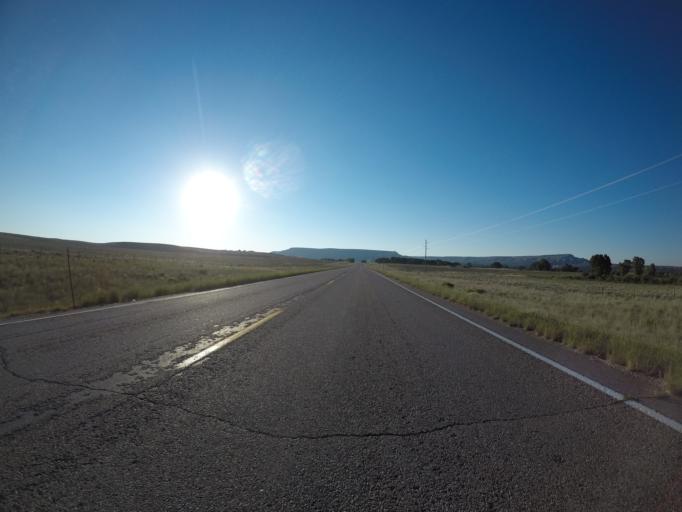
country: US
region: Wyoming
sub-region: Sublette County
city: Marbleton
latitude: 42.5711
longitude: -109.9667
